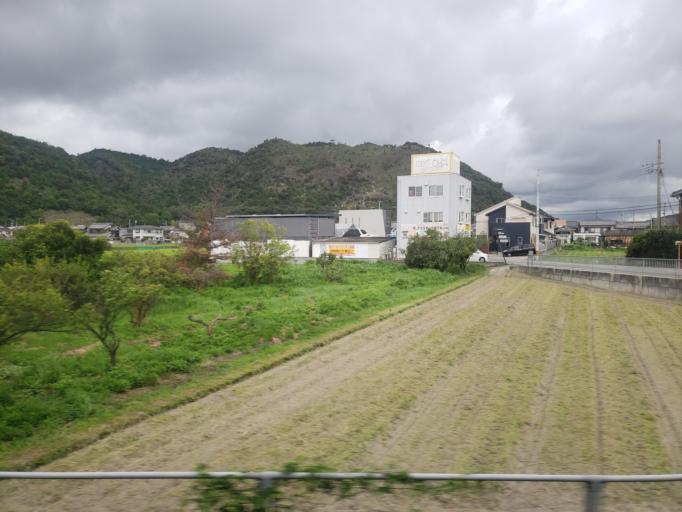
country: JP
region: Hyogo
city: Himeji
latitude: 34.8108
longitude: 134.6282
